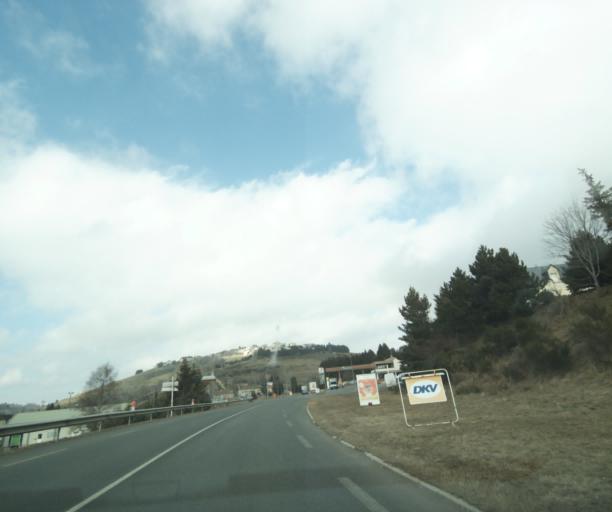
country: FR
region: Languedoc-Roussillon
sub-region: Departement de la Lozere
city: Langogne
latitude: 44.6310
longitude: 3.6757
